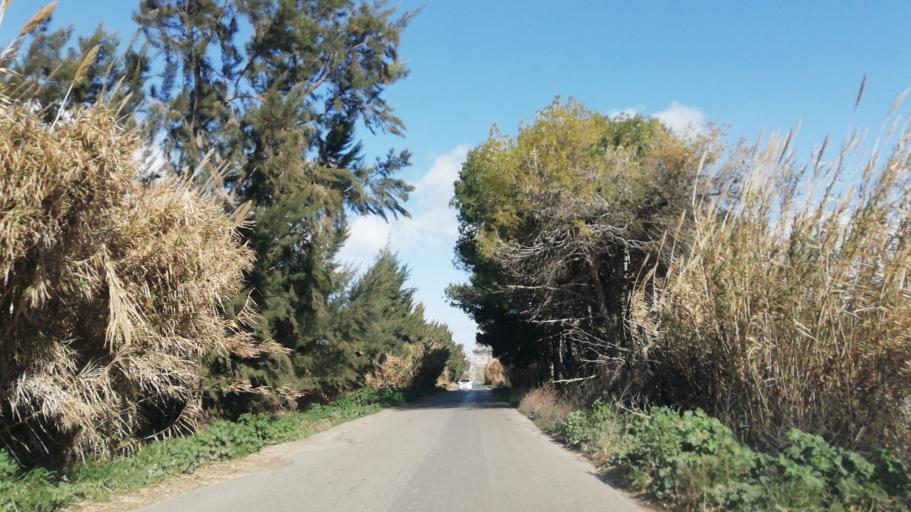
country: DZ
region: Oran
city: Es Senia
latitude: 35.6212
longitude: -0.6615
